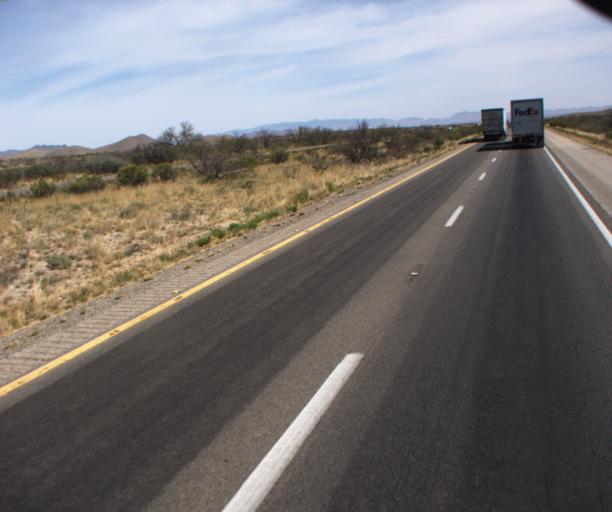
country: US
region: Arizona
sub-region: Cochise County
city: Willcox
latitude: 32.1259
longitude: -110.0122
